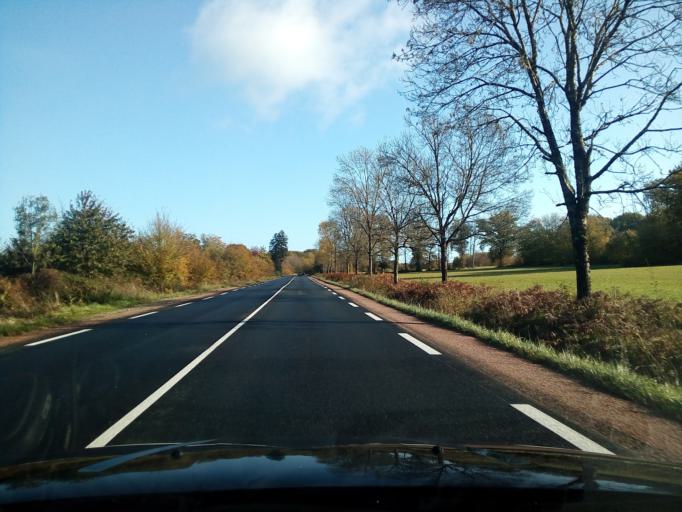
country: FR
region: Limousin
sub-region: Departement de la Haute-Vienne
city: Magnac-Laval
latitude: 46.1775
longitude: 1.1554
